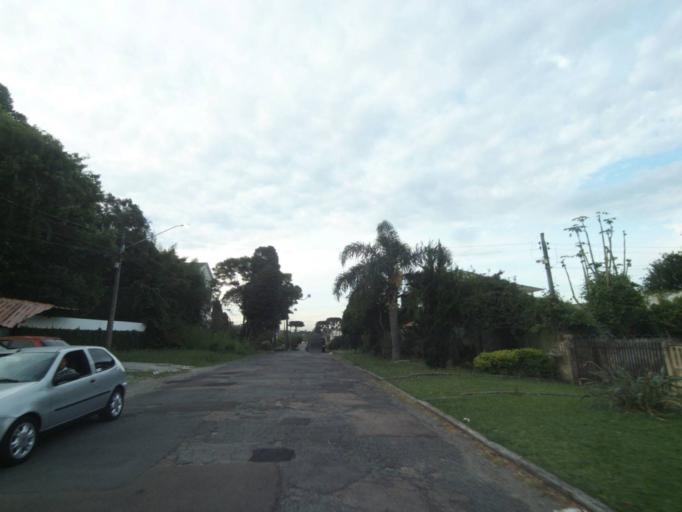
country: BR
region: Parana
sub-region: Curitiba
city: Curitiba
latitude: -25.4320
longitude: -49.2373
